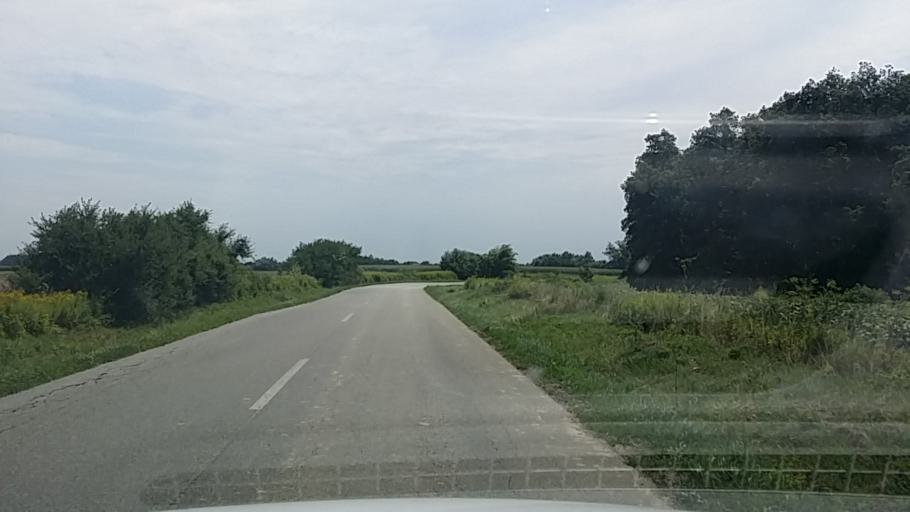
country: HU
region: Zala
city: Becsehely
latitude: 46.4093
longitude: 16.7806
